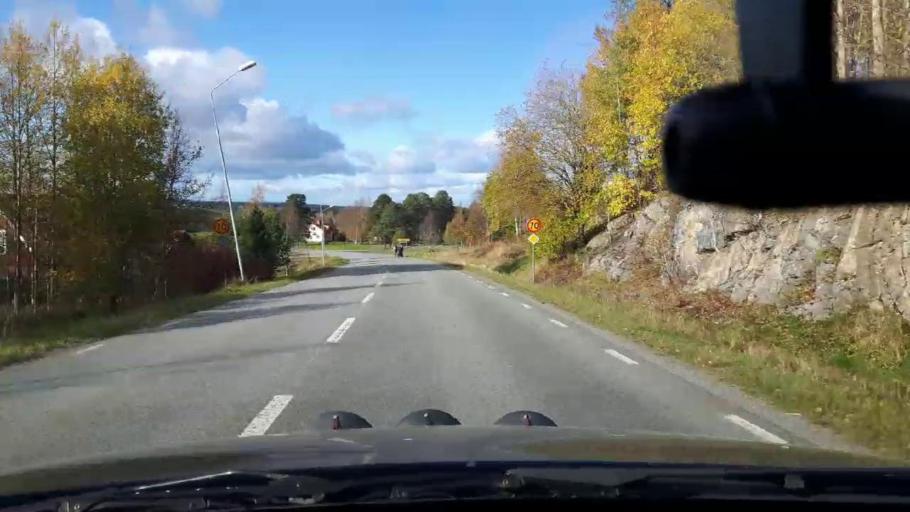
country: SE
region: Jaemtland
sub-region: Bergs Kommun
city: Hoverberg
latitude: 62.9982
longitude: 14.3906
